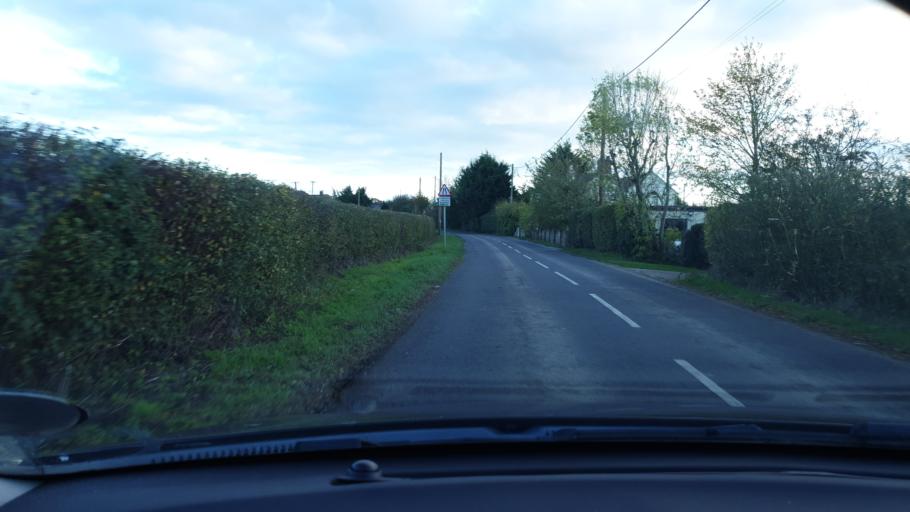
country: GB
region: England
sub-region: Essex
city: Little Clacton
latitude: 51.8977
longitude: 1.1456
